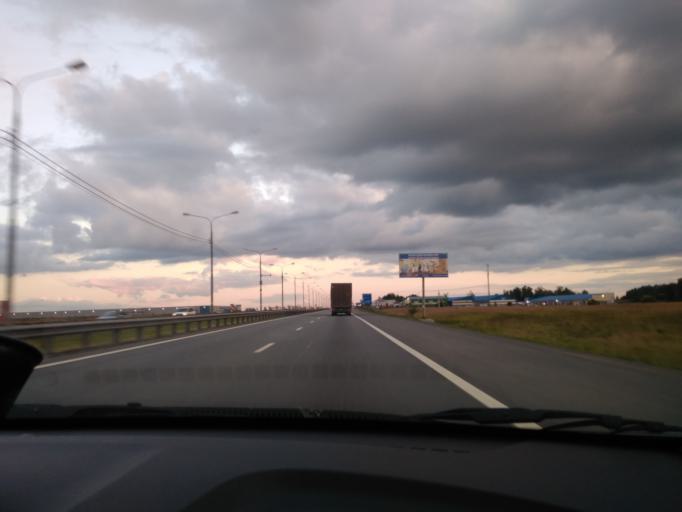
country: RU
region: Moskovskaya
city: Zhukovskiy
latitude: 55.4982
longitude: 38.1482
